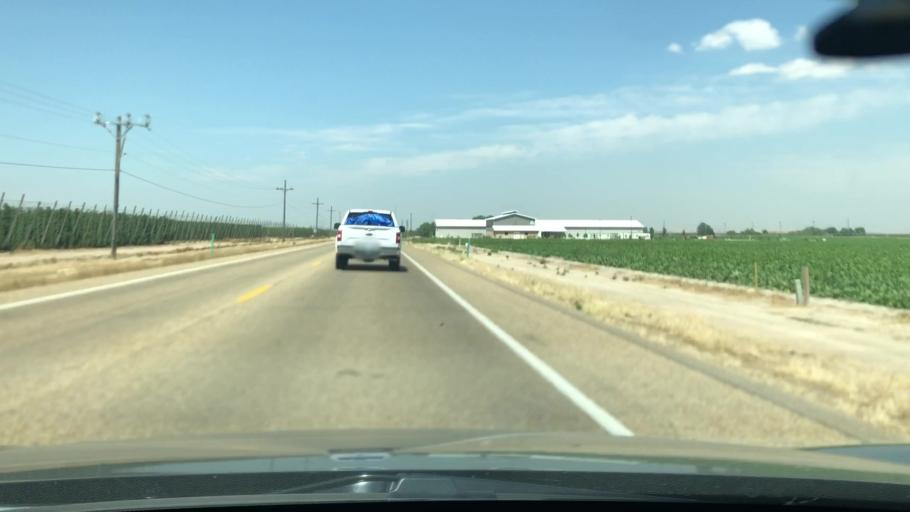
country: US
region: Idaho
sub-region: Canyon County
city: Wilder
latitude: 43.7020
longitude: -116.9120
